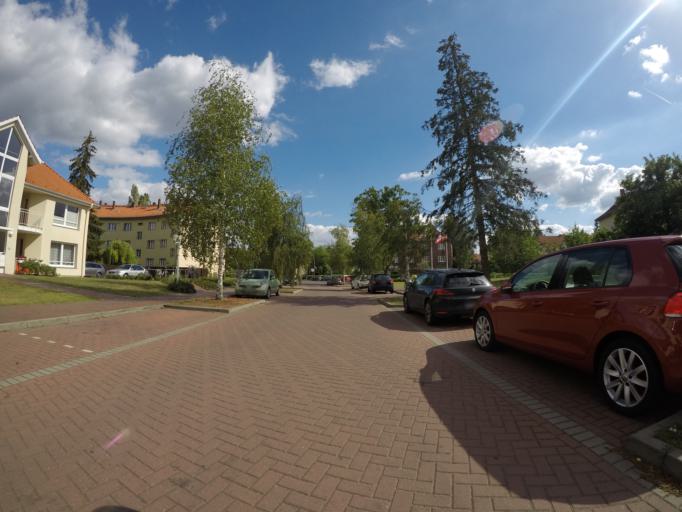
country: DE
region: Berlin
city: Zehlendorf Bezirk
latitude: 52.4389
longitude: 13.2688
